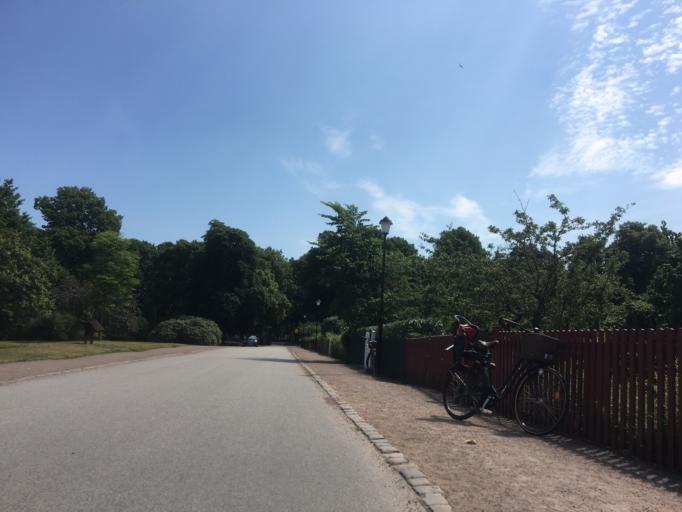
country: SE
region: Skane
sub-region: Landskrona
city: Landskrona
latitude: 55.8739
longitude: 12.8287
